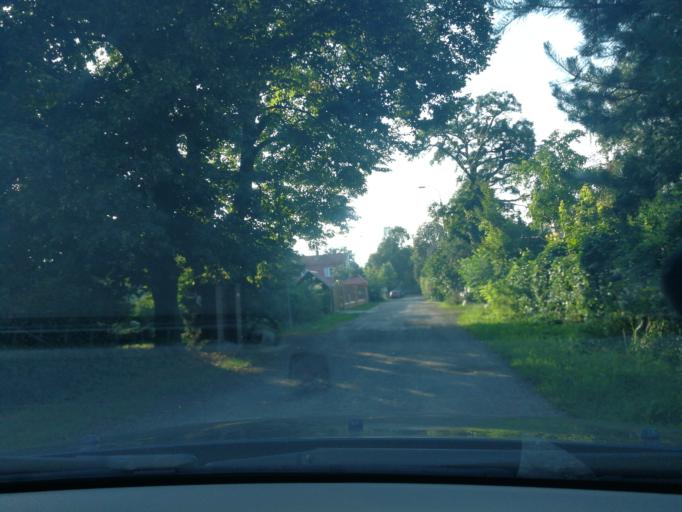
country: PL
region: Masovian Voivodeship
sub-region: Powiat pruszkowski
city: Brwinow
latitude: 52.1360
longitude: 20.7125
